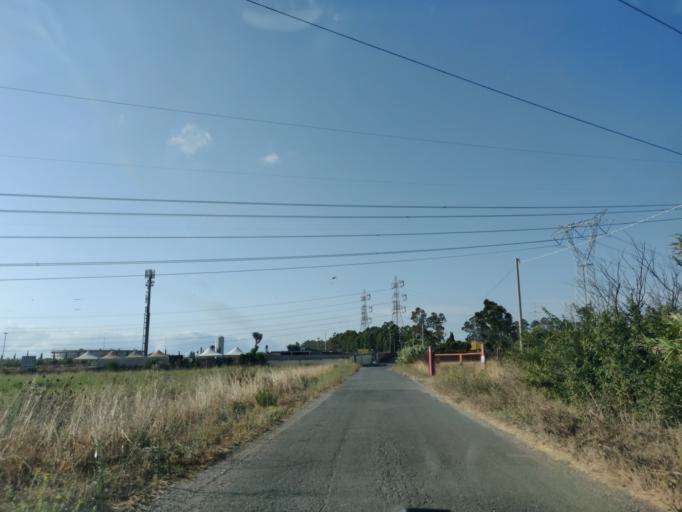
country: IT
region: Latium
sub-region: Citta metropolitana di Roma Capitale
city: Aurelia
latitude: 42.1284
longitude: 11.7676
